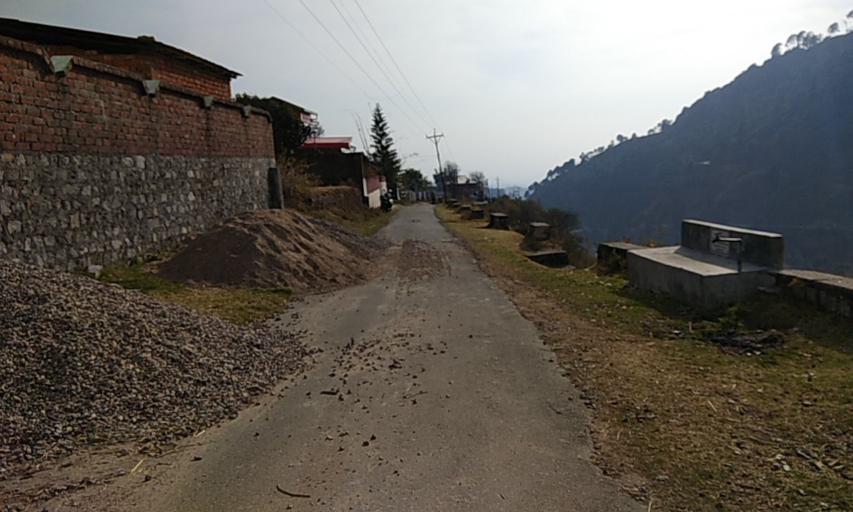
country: IN
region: Himachal Pradesh
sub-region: Kangra
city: Palampur
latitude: 32.1390
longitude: 76.5371
